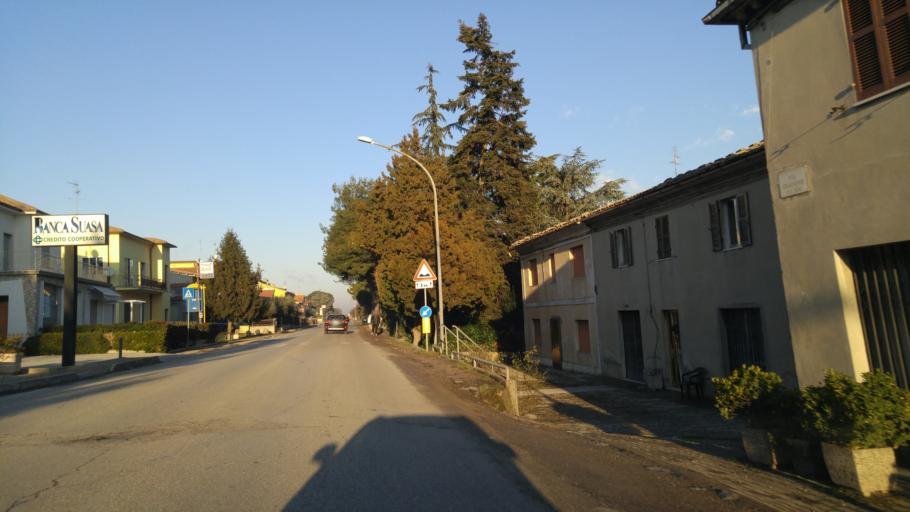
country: IT
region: The Marches
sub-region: Provincia di Pesaro e Urbino
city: Monte Porzio
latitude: 43.6978
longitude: 13.0595
